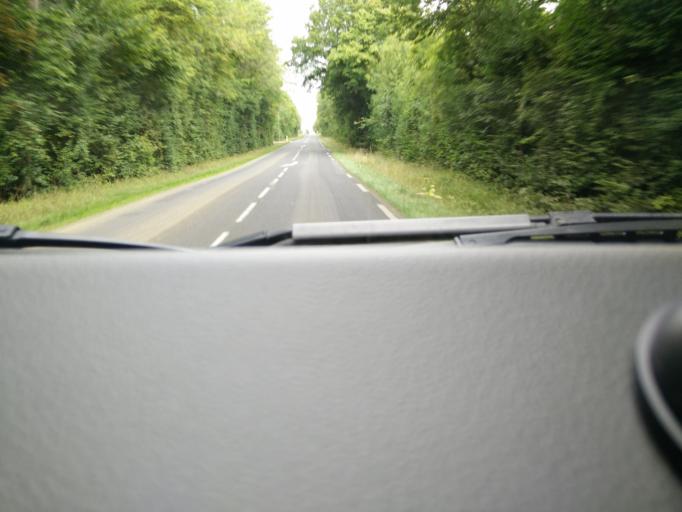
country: FR
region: Lorraine
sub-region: Departement de Meurthe-et-Moselle
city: Montauville
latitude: 48.9201
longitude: 5.9145
